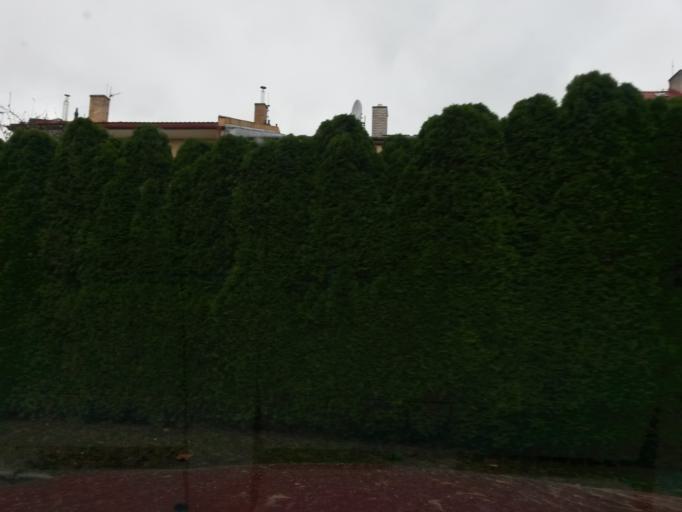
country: SK
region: Kosicky
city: Kosice
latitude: 48.7065
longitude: 21.2236
